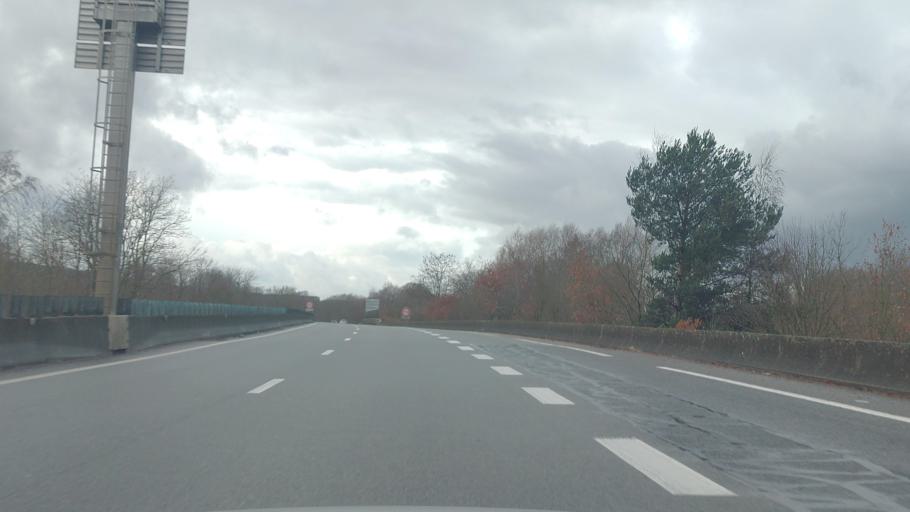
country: FR
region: Picardie
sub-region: Departement de l'Oise
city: Clermont
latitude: 49.3894
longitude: 2.4091
